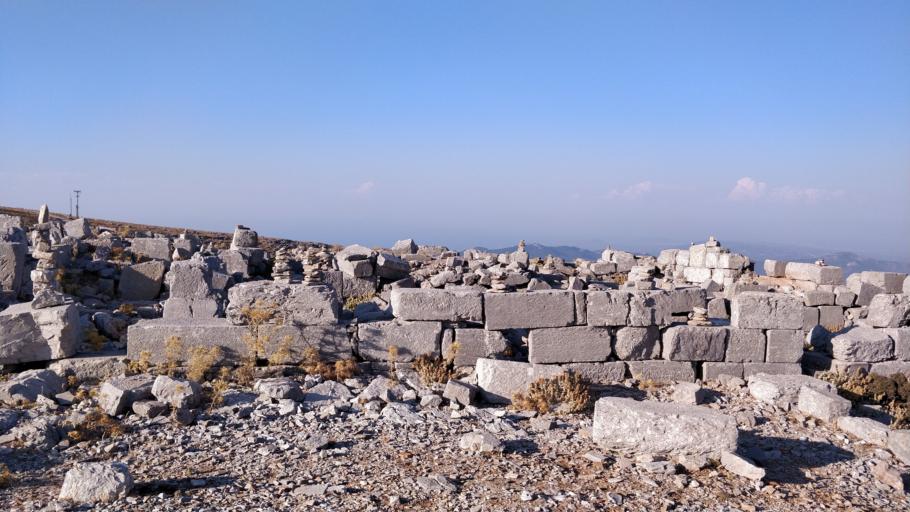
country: GR
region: South Aegean
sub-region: Nomos Dodekanisou
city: Emponas
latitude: 36.2065
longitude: 27.8645
